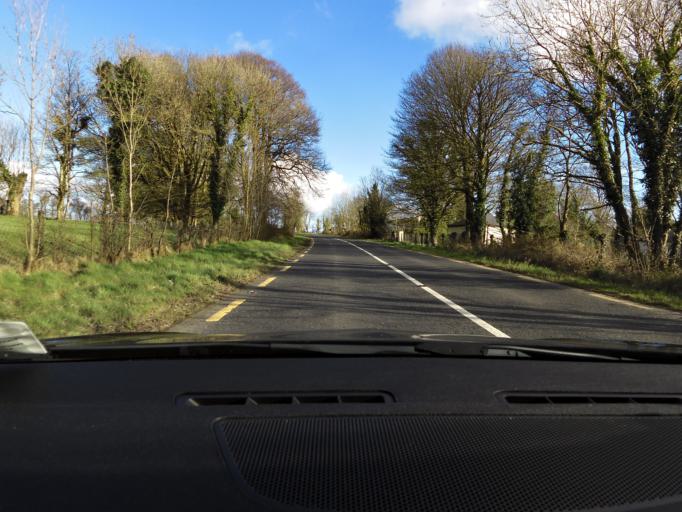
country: IE
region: Connaught
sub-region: Roscommon
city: Roscommon
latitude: 53.6560
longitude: -8.2618
